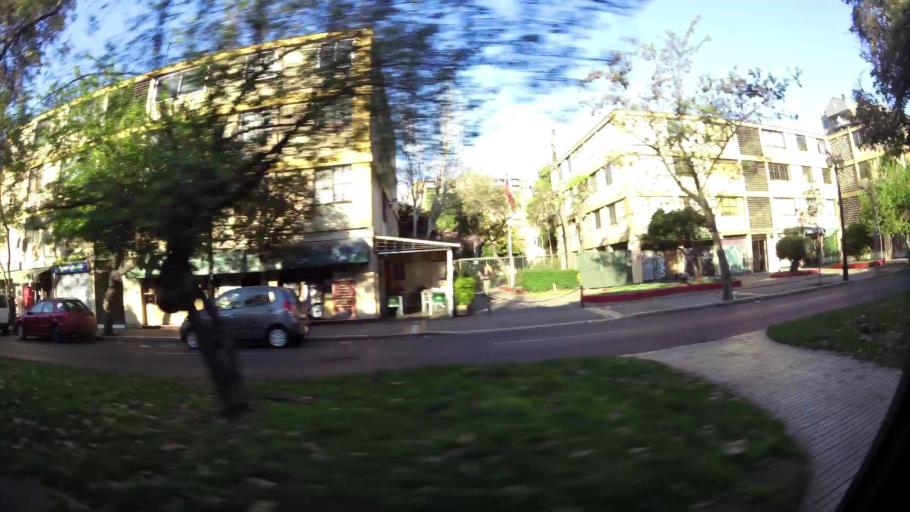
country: CL
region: Santiago Metropolitan
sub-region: Provincia de Santiago
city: Santiago
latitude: -33.4432
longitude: -70.6679
